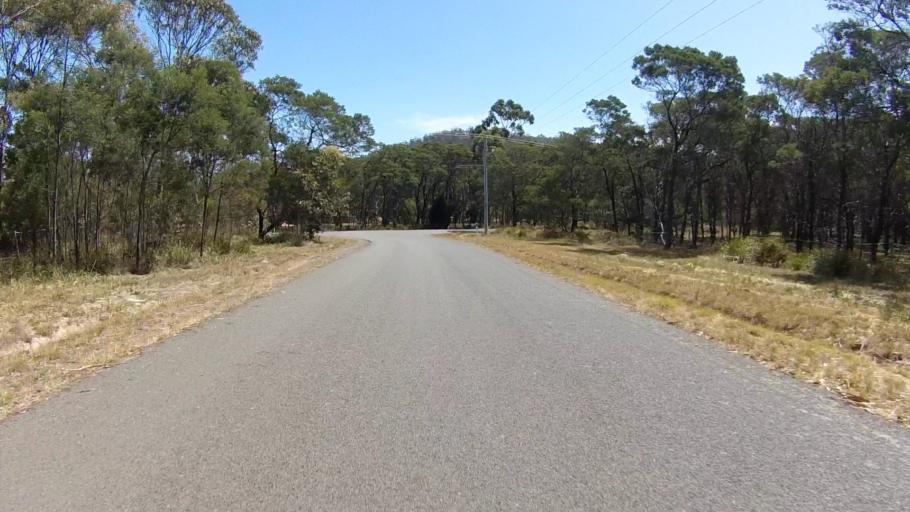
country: AU
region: Tasmania
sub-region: Clarence
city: Sandford
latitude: -42.9645
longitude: 147.4761
